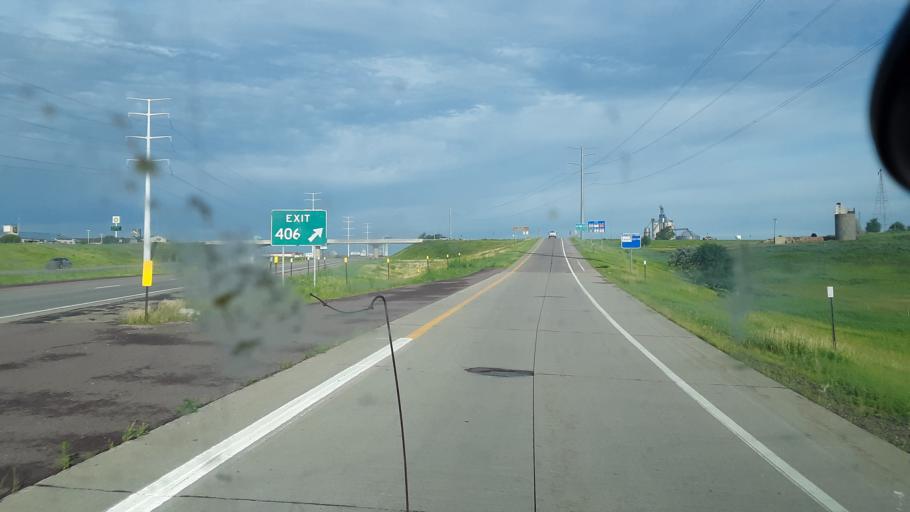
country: US
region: South Dakota
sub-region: Minnehaha County
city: Brandon
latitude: 43.6087
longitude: -96.5686
